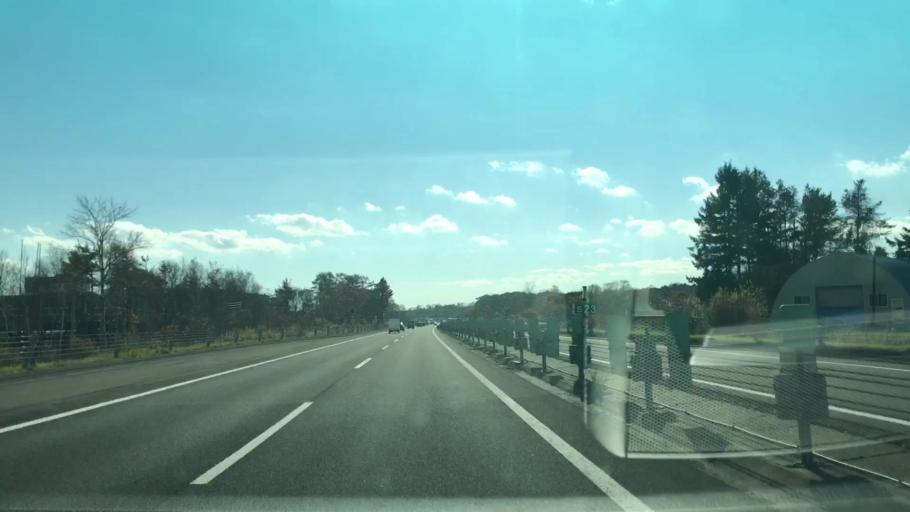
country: JP
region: Hokkaido
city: Kitahiroshima
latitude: 42.9004
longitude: 141.5505
